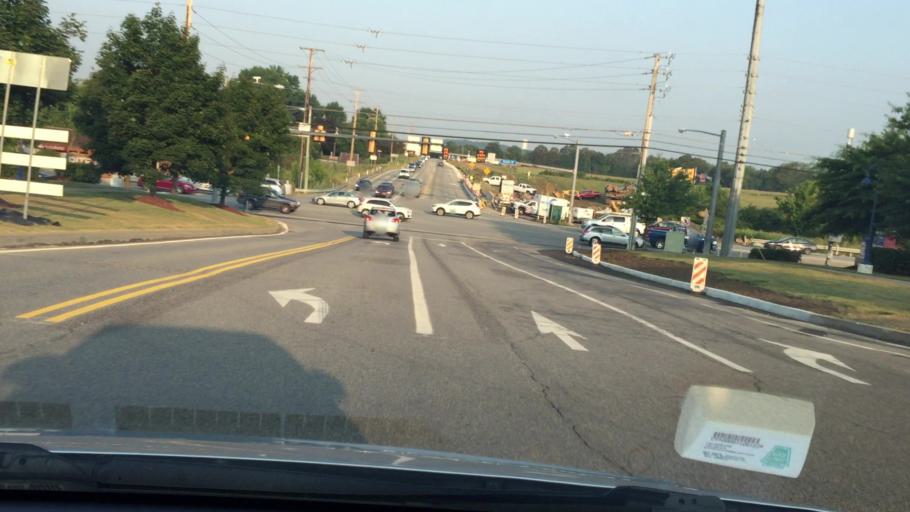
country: US
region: Pennsylvania
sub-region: Butler County
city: Cranberry Township
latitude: 40.6991
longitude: -80.1036
